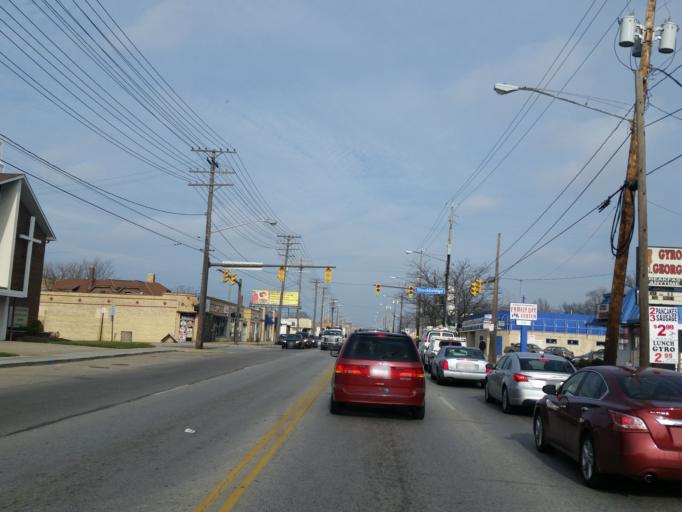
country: US
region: Ohio
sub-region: Cuyahoga County
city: Warrensville Heights
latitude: 41.4511
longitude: -81.5649
